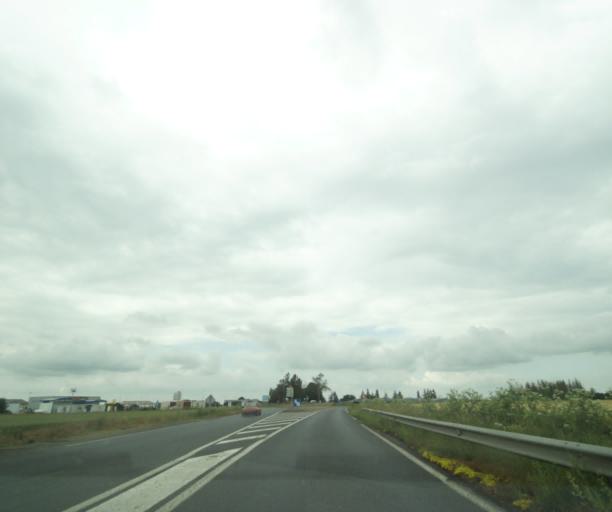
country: FR
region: Poitou-Charentes
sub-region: Departement des Deux-Sevres
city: Saint-Jean-de-Thouars
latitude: 46.9549
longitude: -0.2073
